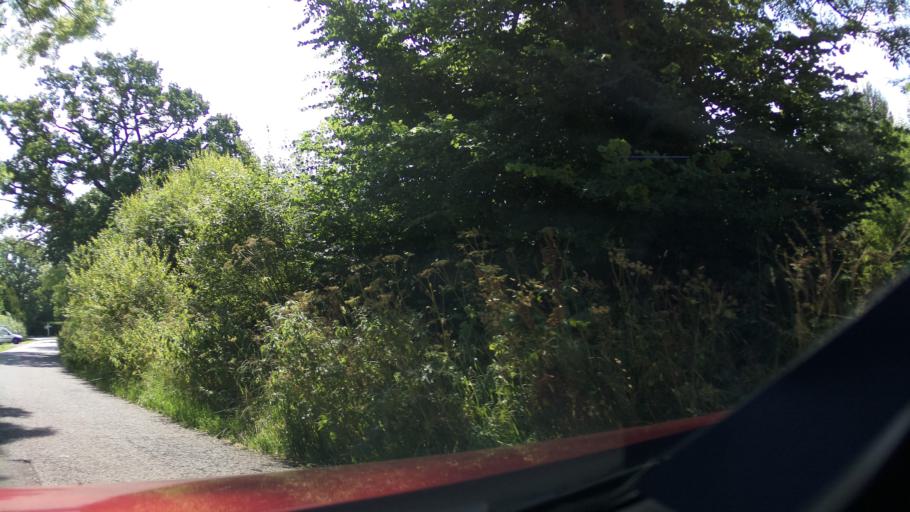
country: GB
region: England
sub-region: Wiltshire
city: Minety
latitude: 51.6174
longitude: -1.9941
